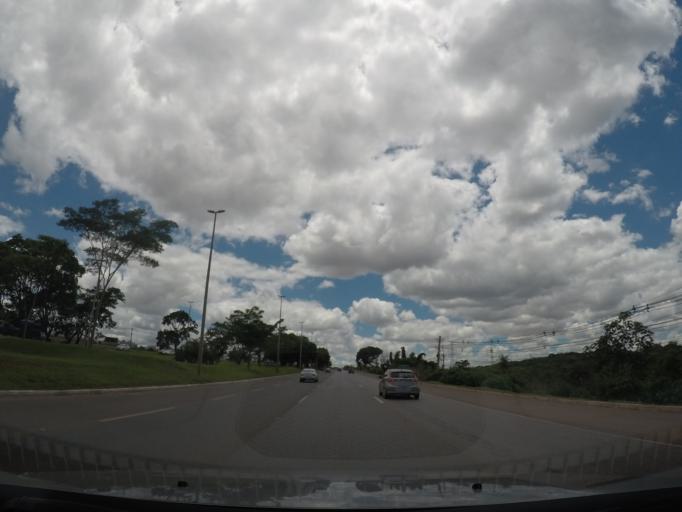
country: BR
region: Federal District
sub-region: Brasilia
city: Brasilia
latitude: -15.7307
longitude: -47.9113
